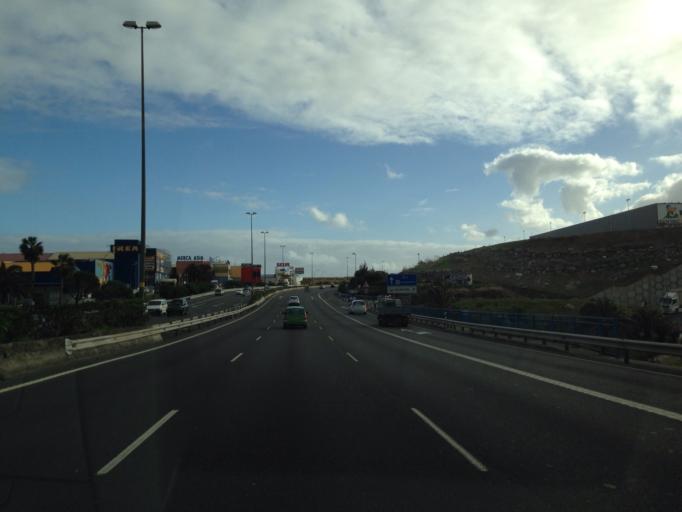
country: ES
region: Canary Islands
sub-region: Provincia de Las Palmas
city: Telde
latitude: 27.9802
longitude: -15.3913
